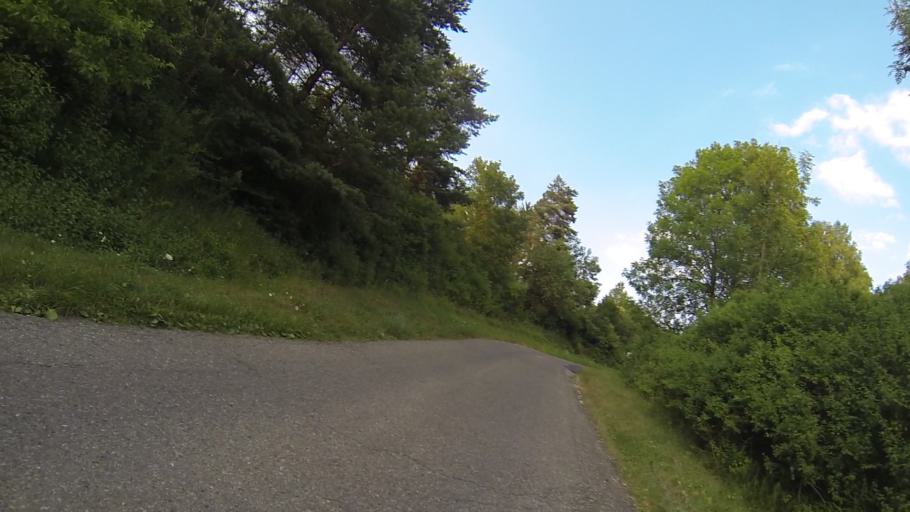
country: DE
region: Baden-Wuerttemberg
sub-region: Tuebingen Region
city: Dornstadt
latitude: 48.4192
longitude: 9.9249
